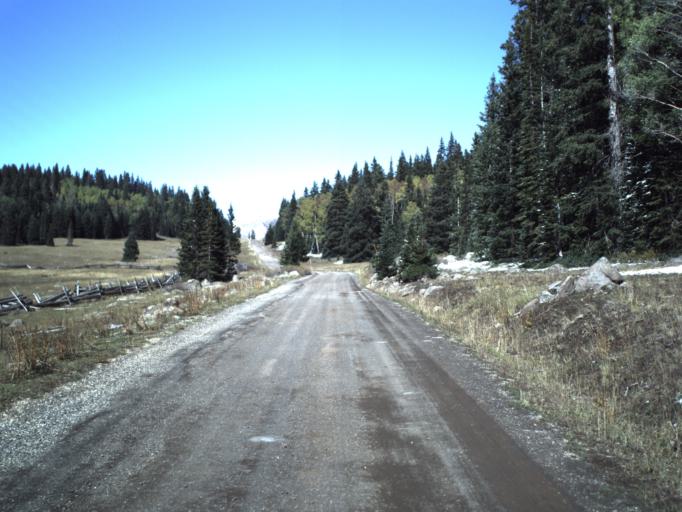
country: US
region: Utah
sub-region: Piute County
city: Junction
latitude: 38.2926
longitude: -112.3596
